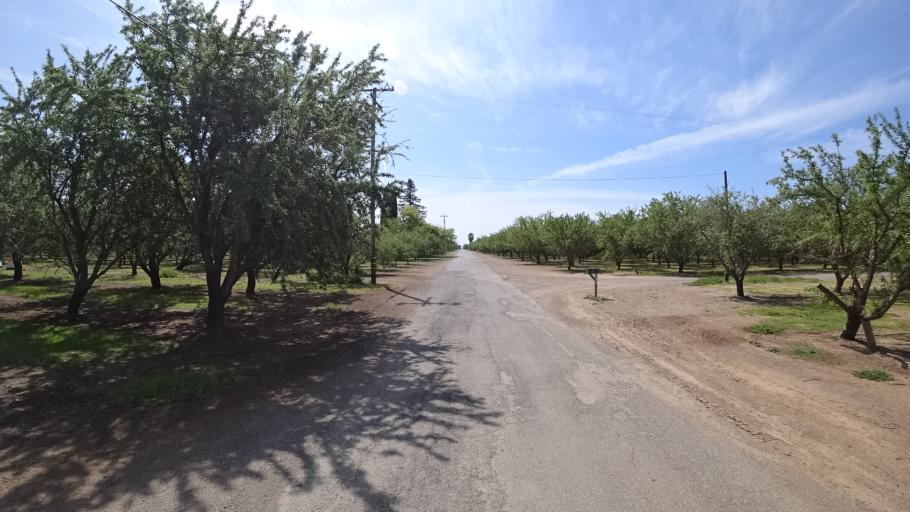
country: US
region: California
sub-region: Glenn County
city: Hamilton City
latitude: 39.8006
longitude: -122.0664
